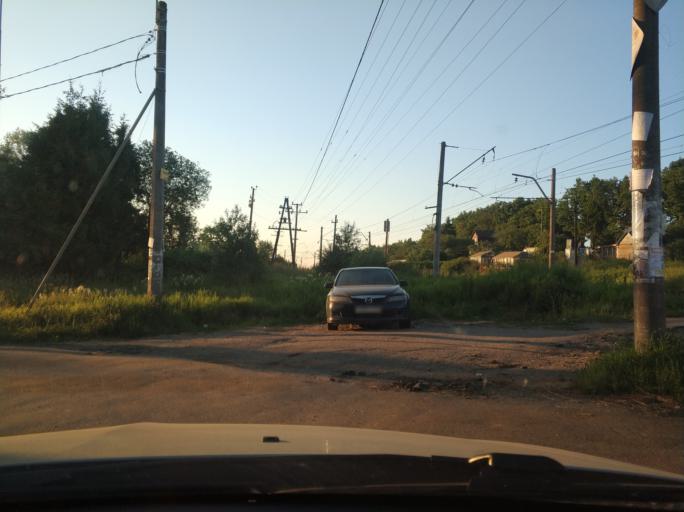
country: RU
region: St.-Petersburg
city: Gorelovo
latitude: 59.7526
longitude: 30.1161
